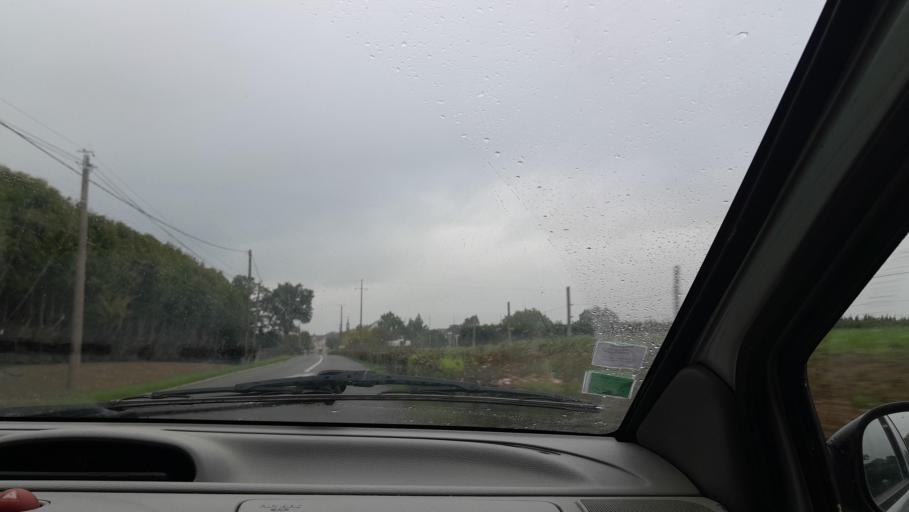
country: FR
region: Pays de la Loire
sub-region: Departement de la Mayenne
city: Congrier
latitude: 47.8345
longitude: -1.1400
